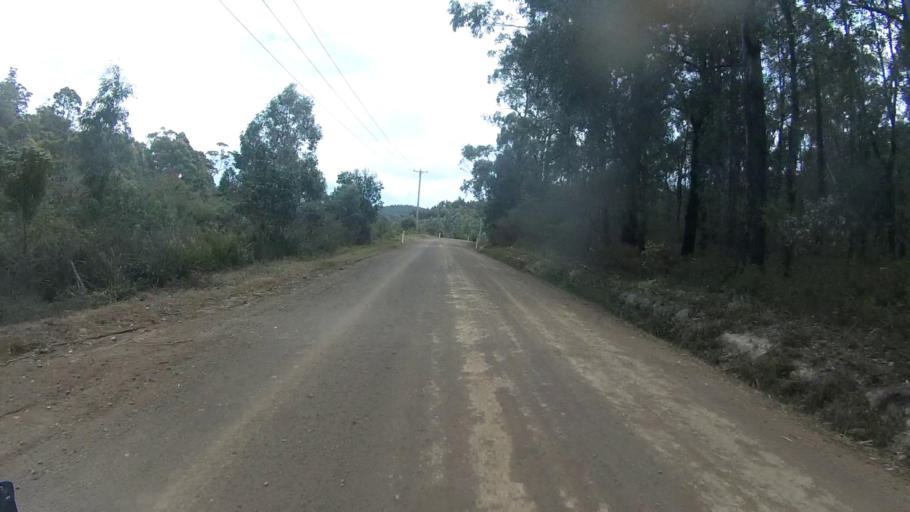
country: AU
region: Tasmania
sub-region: Sorell
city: Sorell
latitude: -42.7609
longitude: 147.8023
